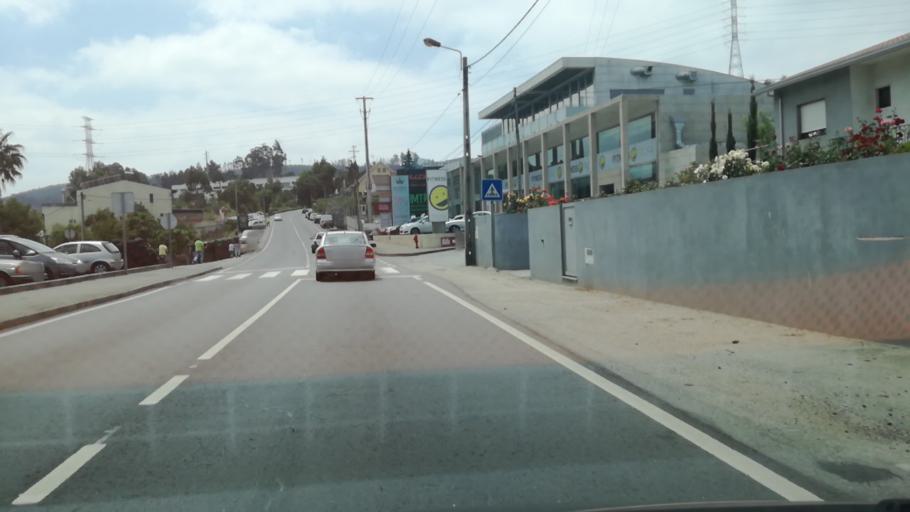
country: PT
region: Porto
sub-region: Trofa
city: Sao Romao do Coronado
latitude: 41.3115
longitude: -8.5809
